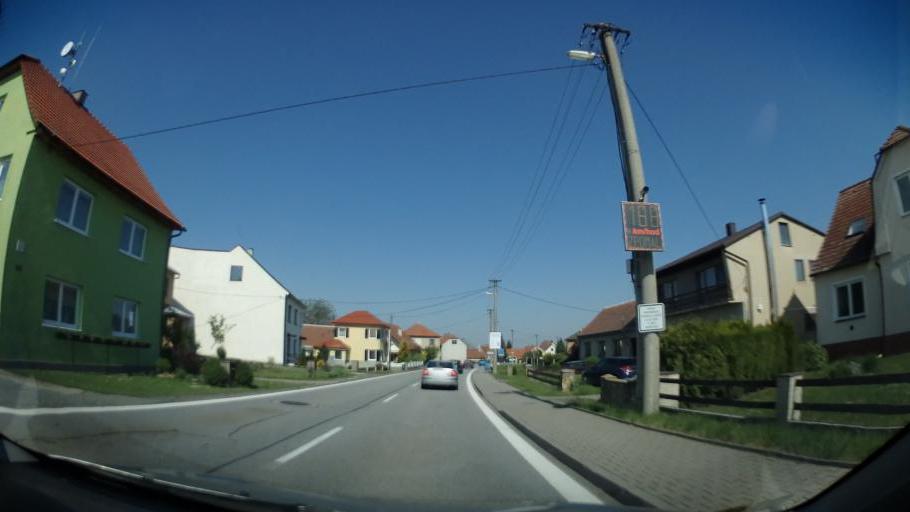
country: CZ
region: South Moravian
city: Zbraslav
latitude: 49.1889
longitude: 16.2578
